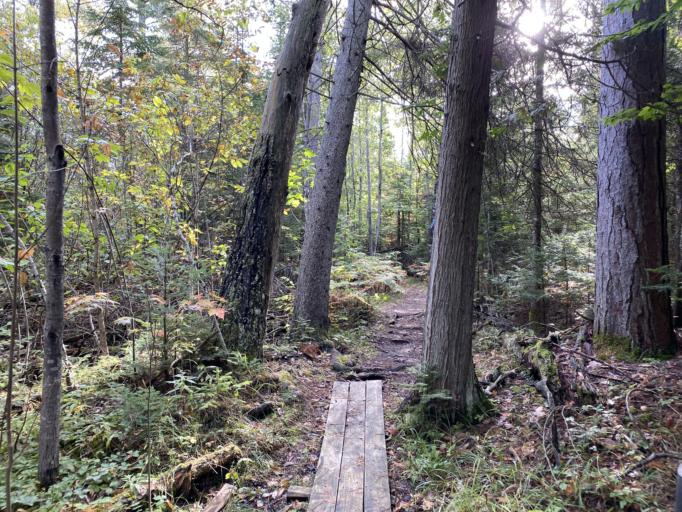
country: US
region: Michigan
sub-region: Mackinac County
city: Saint Ignace
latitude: 45.7427
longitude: -84.8925
